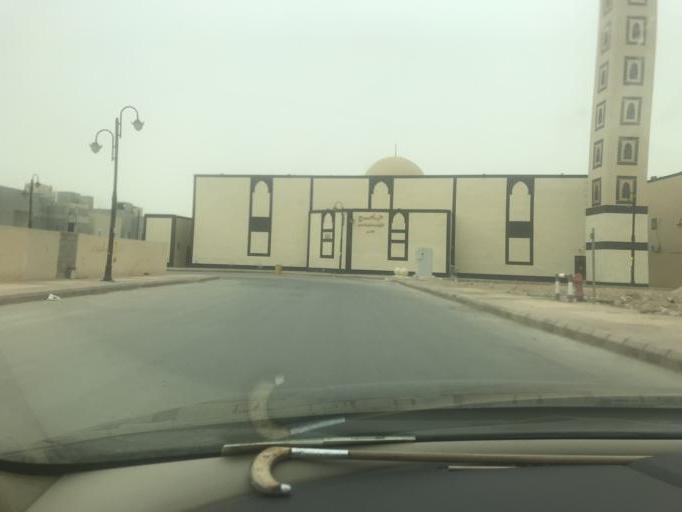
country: SA
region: Ar Riyad
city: Riyadh
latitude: 24.7367
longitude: 46.7848
